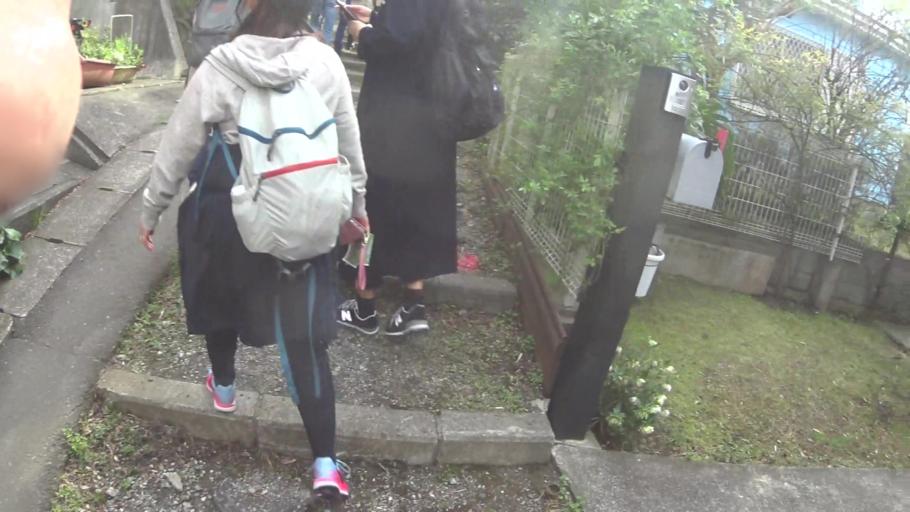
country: JP
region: Kanagawa
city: Kamakura
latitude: 35.3224
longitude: 139.5134
